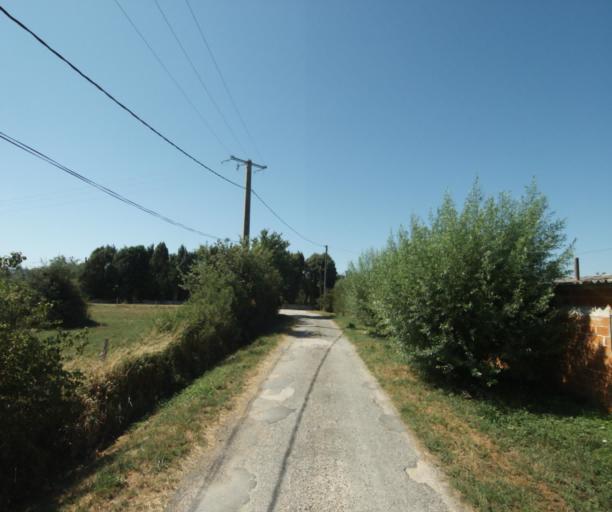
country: FR
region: Midi-Pyrenees
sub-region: Departement de la Haute-Garonne
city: Revel
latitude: 43.4618
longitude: 1.9840
